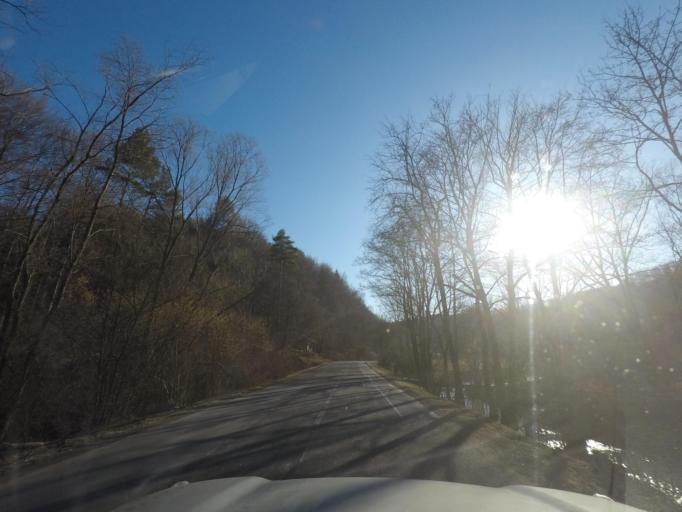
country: SK
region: Presovsky
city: Medzilaborce
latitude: 49.2744
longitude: 21.8050
